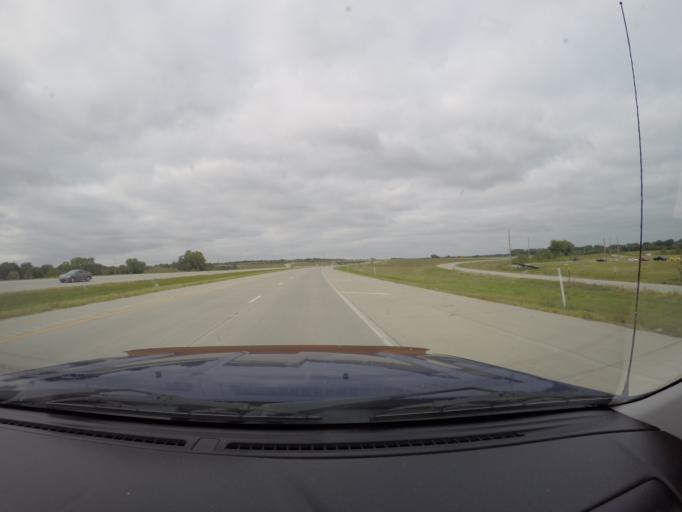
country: US
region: Kansas
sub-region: Riley County
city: Ogden
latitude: 39.1096
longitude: -96.6995
